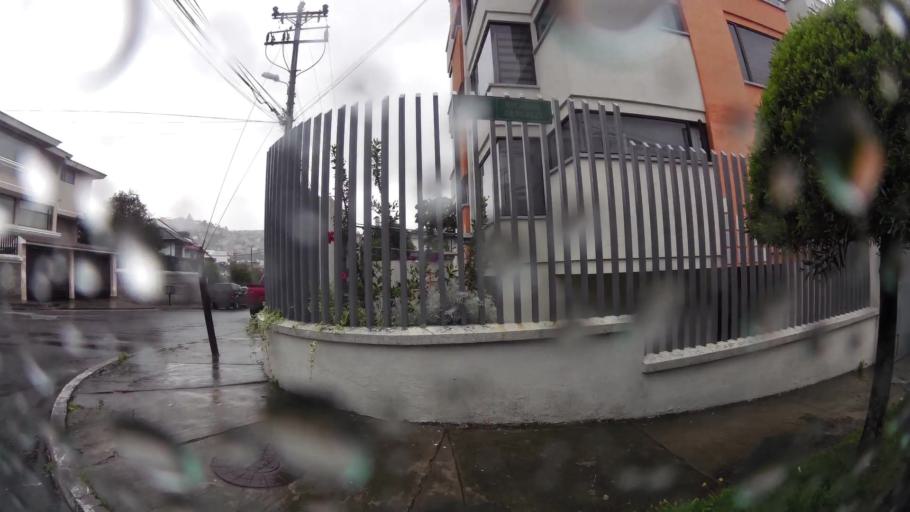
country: EC
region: Pichincha
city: Quito
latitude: -0.1035
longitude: -78.5031
